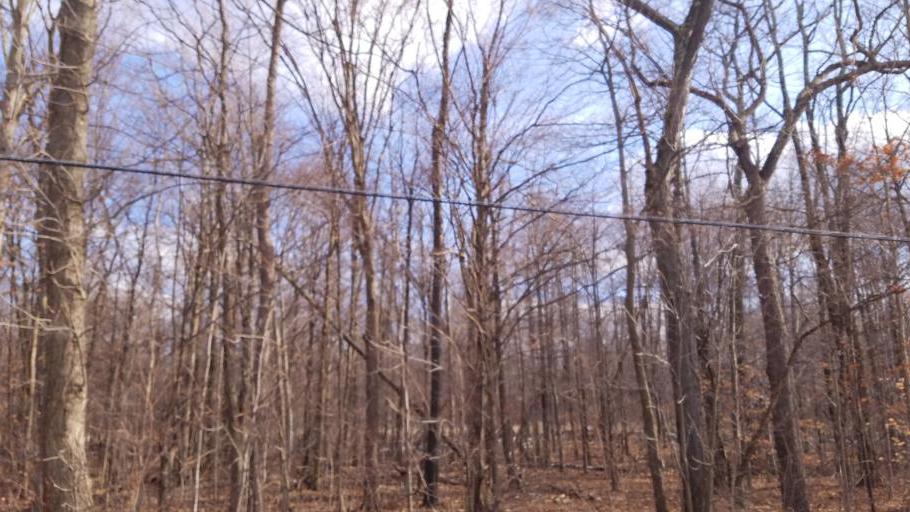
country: US
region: Ohio
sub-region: Crawford County
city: Crestline
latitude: 40.7795
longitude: -82.6757
